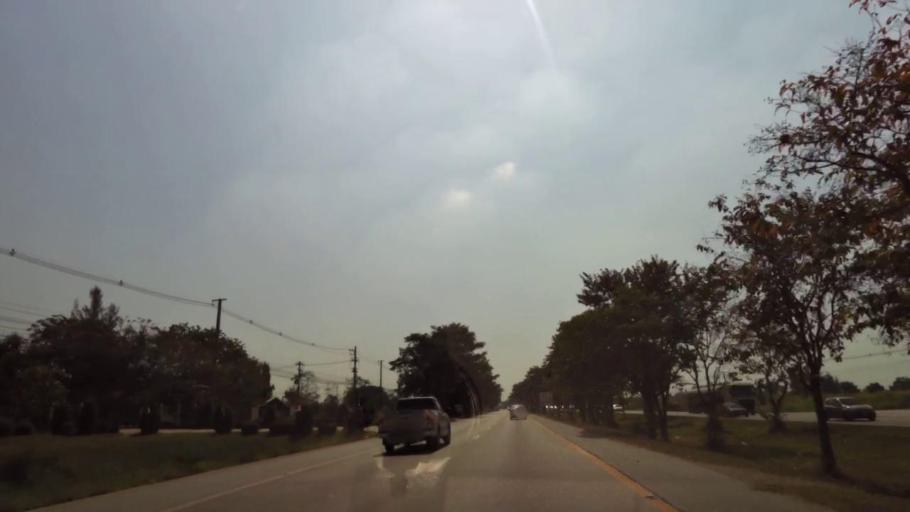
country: TH
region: Phichit
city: Wachira Barami
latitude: 16.5180
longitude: 100.1429
